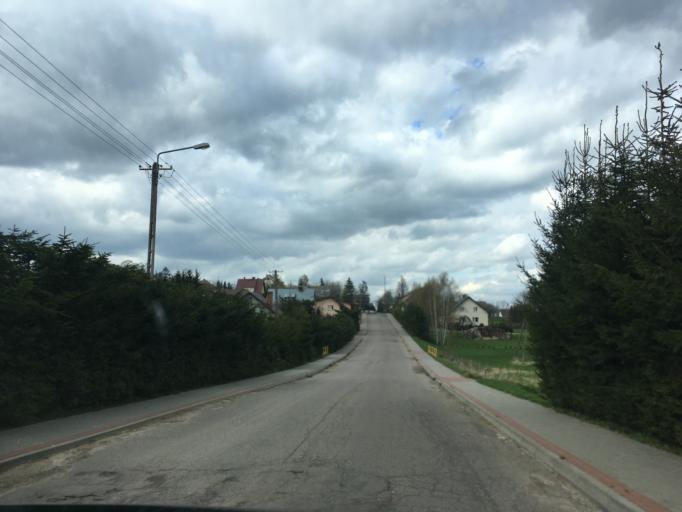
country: PL
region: Podlasie
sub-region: Suwalki
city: Suwalki
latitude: 54.3651
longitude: 22.8689
